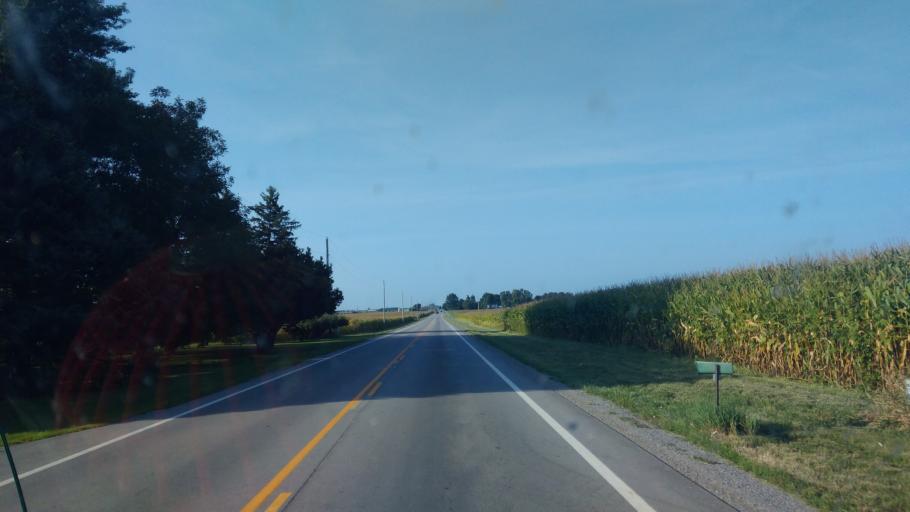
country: US
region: Ohio
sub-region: Wyandot County
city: Upper Sandusky
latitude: 40.8732
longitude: -83.2779
